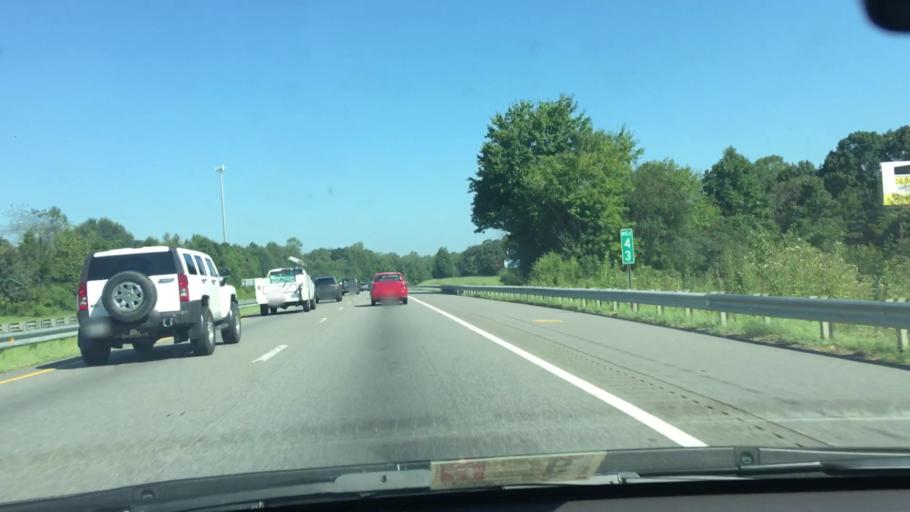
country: US
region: North Carolina
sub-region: Iredell County
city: Troutman
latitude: 35.6924
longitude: -80.8578
